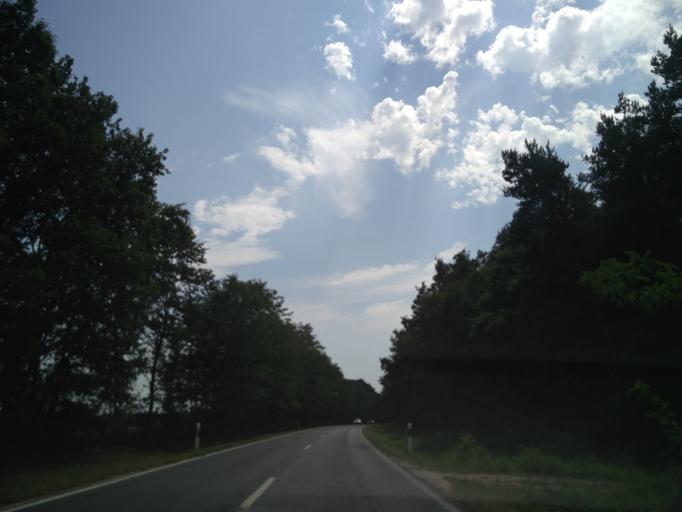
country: HU
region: Zala
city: Zalaegerszeg
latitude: 46.9011
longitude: 16.8578
